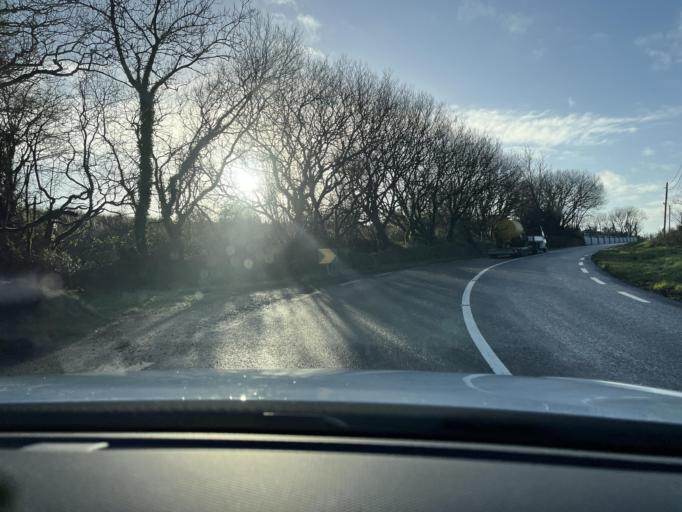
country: IE
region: Connaught
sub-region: County Leitrim
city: Manorhamilton
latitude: 54.2237
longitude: -8.2042
